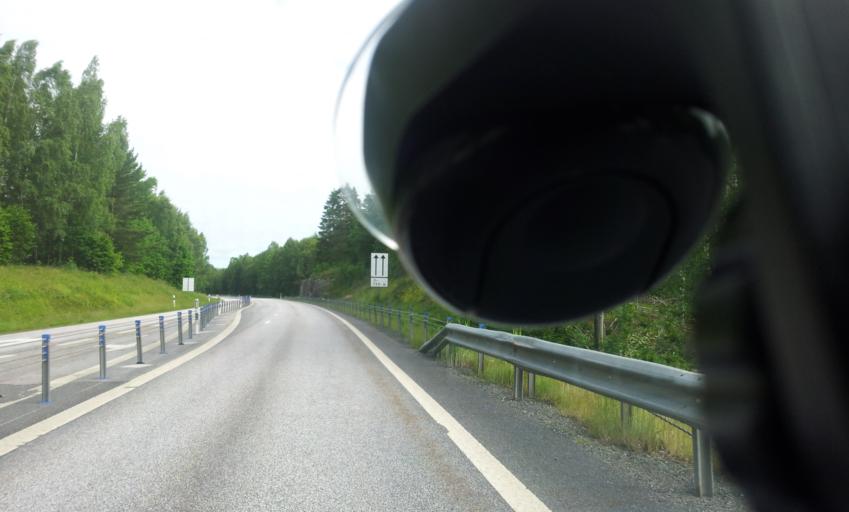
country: SE
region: OEstergoetland
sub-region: Valdemarsviks Kommun
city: Valdemarsvik
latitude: 58.1112
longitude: 16.5430
